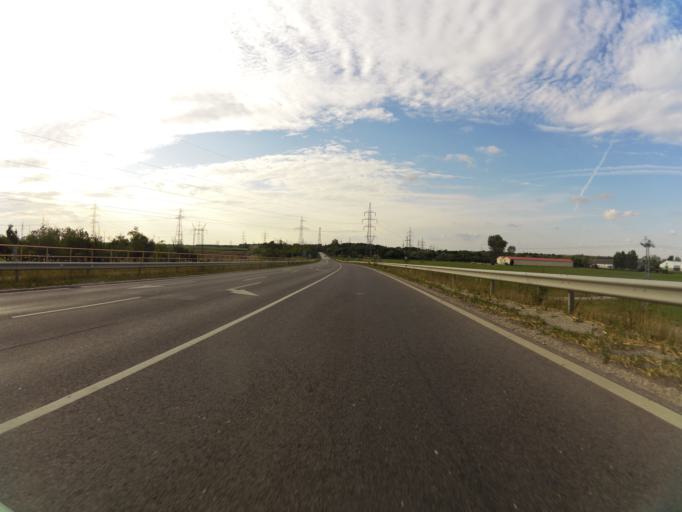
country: HU
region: Csongrad
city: Szeged
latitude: 46.2964
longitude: 20.1341
